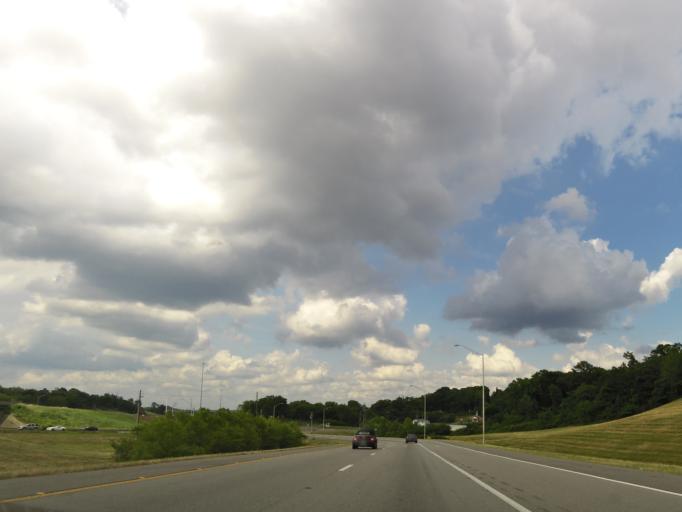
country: US
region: Alabama
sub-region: Jefferson County
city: Birmingham
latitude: 33.5604
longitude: -86.8275
